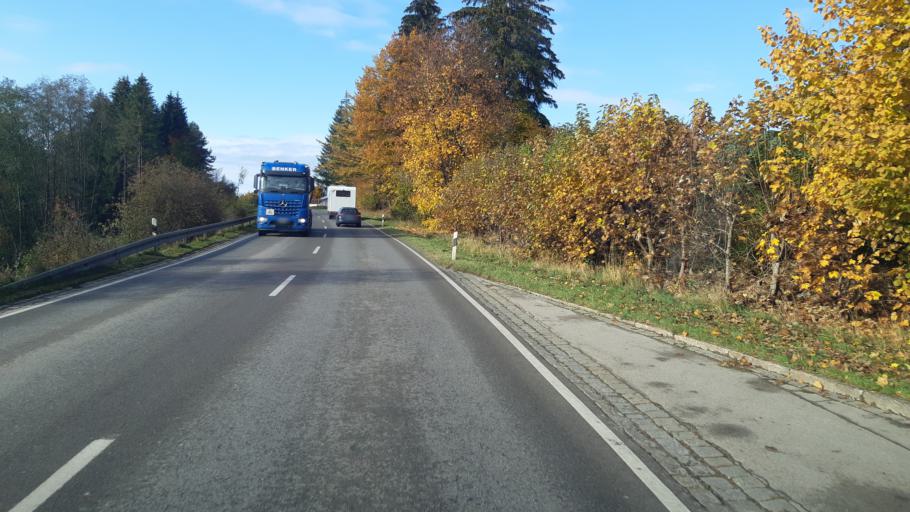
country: DE
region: Bavaria
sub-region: Swabia
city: Marktoberdorf
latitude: 47.7741
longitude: 10.5929
